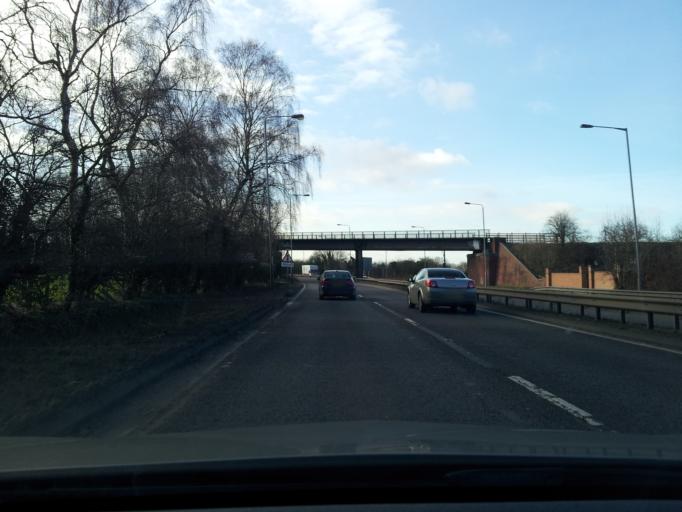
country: GB
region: England
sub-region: Nottinghamshire
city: Radcliffe on Trent
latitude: 52.9406
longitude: -1.0576
